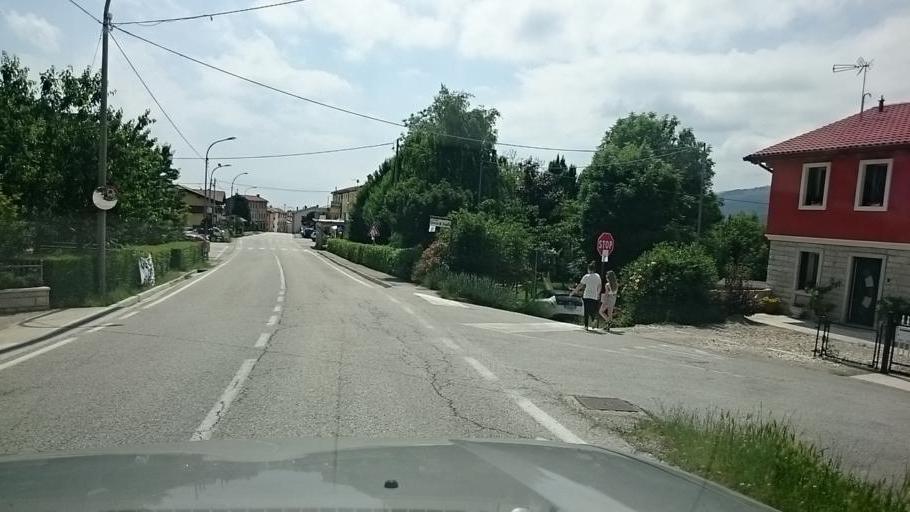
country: IT
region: Veneto
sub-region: Provincia di Vicenza
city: Conco
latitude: 45.8046
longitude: 11.6143
